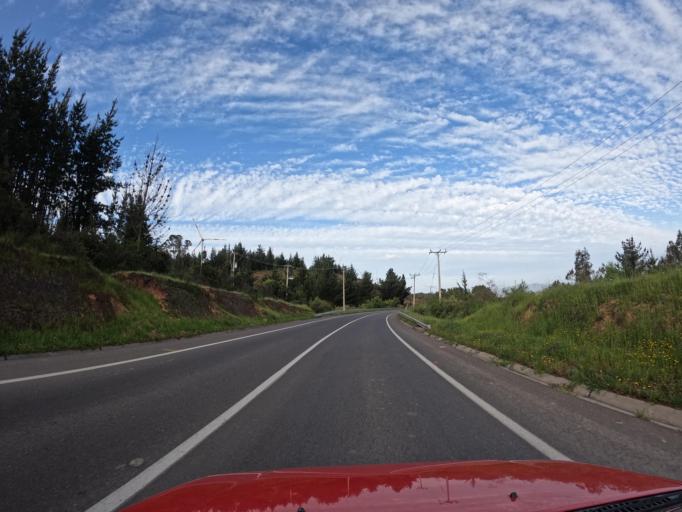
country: CL
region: Valparaiso
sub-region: San Antonio Province
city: San Antonio
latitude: -34.0504
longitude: -71.6214
